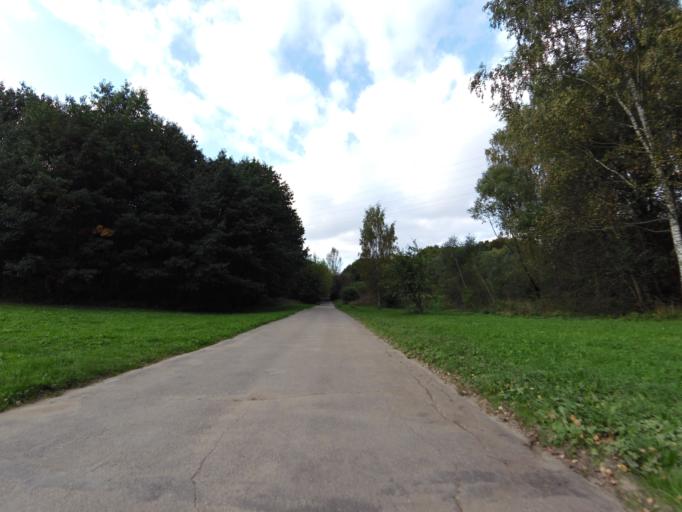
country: LT
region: Vilnius County
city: Seskine
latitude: 54.7069
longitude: 25.2469
